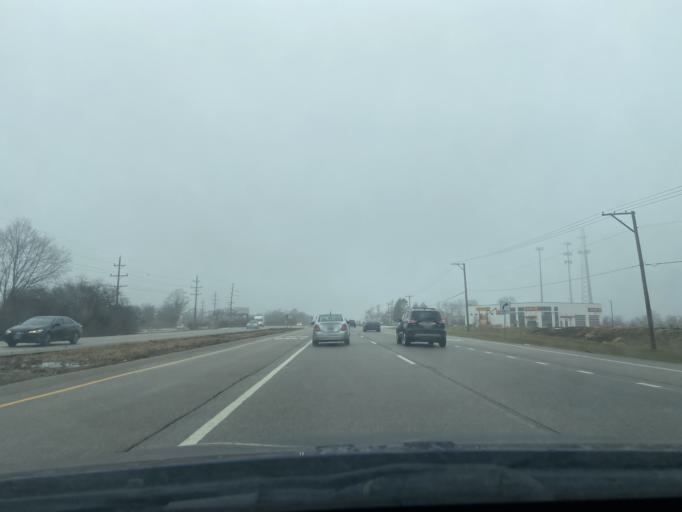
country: US
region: Illinois
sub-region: Lake County
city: Wauconda
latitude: 42.2482
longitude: -88.1349
